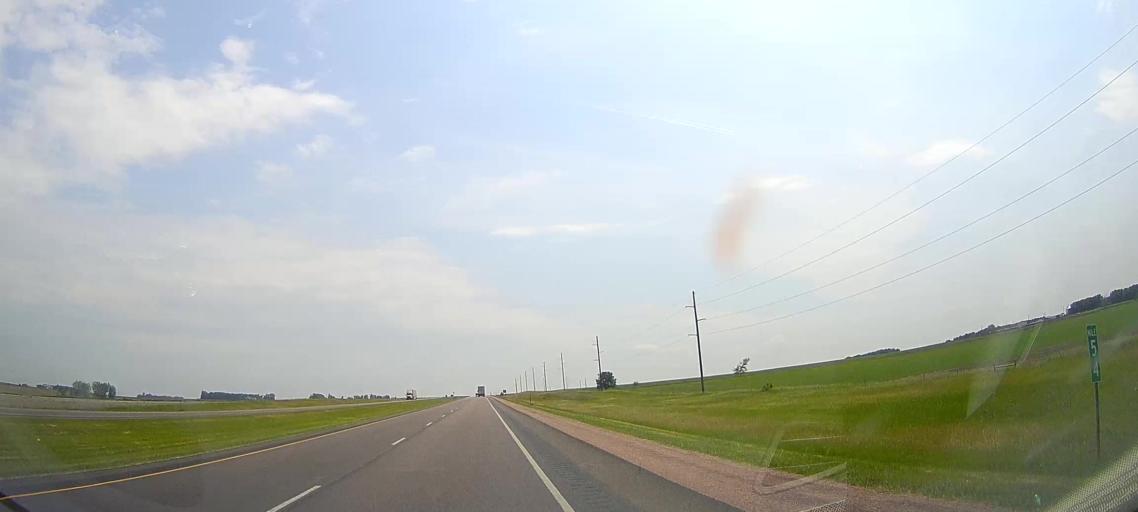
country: US
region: South Dakota
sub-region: Union County
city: Beresford
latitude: 43.1801
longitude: -96.7959
